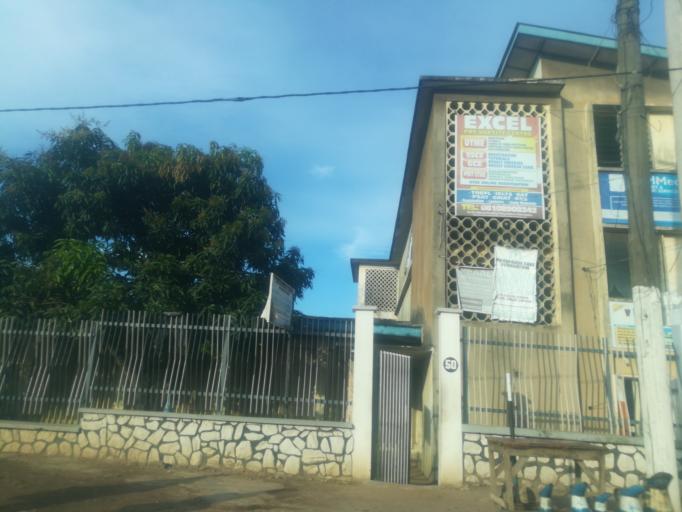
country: NG
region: Oyo
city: Ibadan
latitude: 7.3460
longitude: 3.8842
